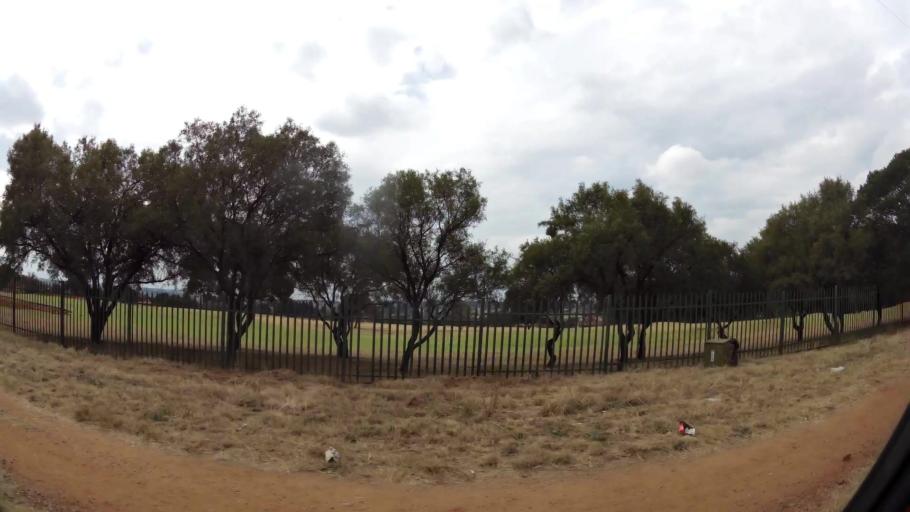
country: ZA
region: Gauteng
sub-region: West Rand District Municipality
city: Muldersdriseloop
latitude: -26.0806
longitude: 27.8638
